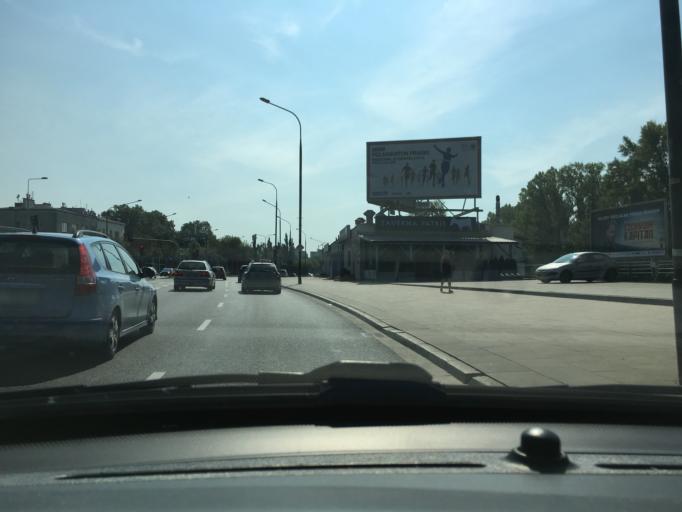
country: PL
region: Masovian Voivodeship
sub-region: Warszawa
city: Praga Polnoc
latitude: 52.2358
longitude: 21.0453
